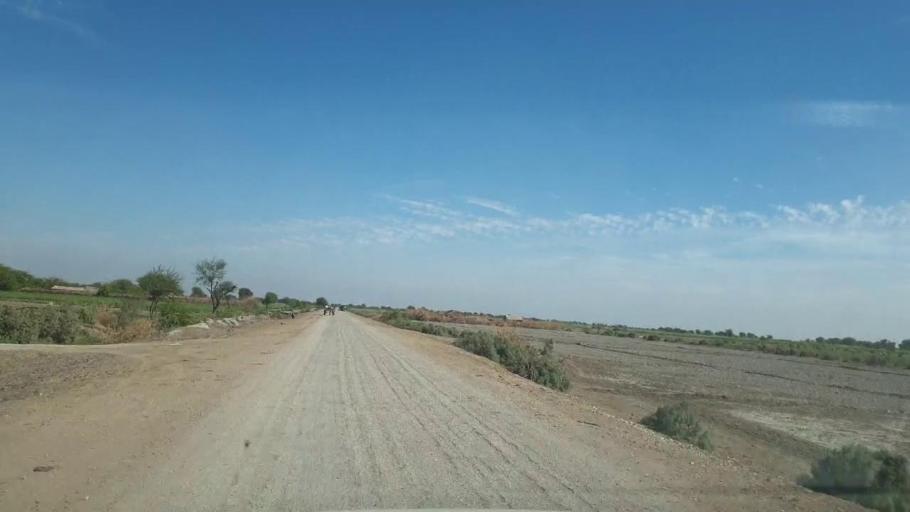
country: PK
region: Sindh
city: Pithoro
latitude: 25.5784
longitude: 69.2961
